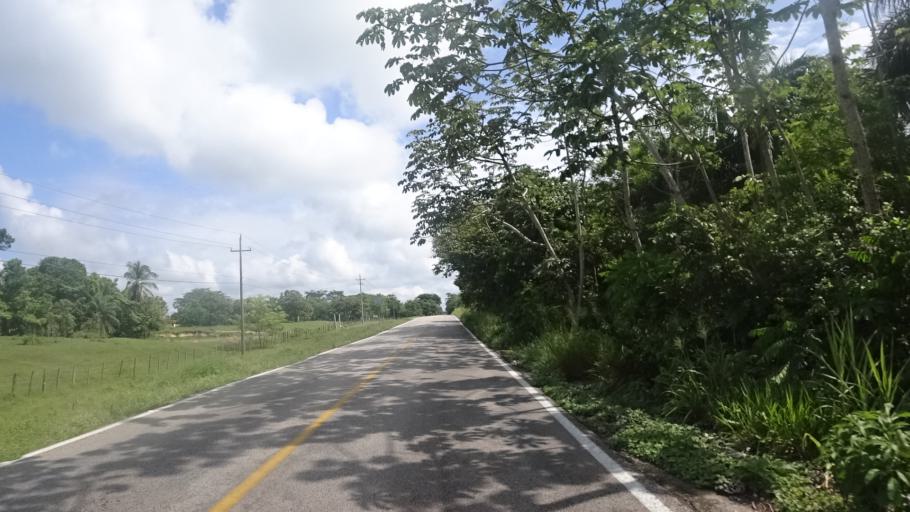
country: MX
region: Chiapas
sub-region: Catazaja
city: Catazaja
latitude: 17.6671
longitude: -92.0349
